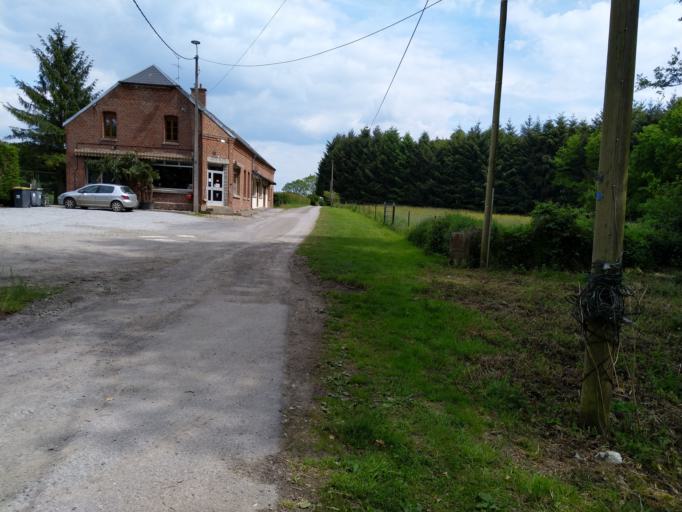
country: FR
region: Picardie
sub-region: Departement de l'Aisne
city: Wassigny
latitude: 50.0466
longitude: 3.6444
